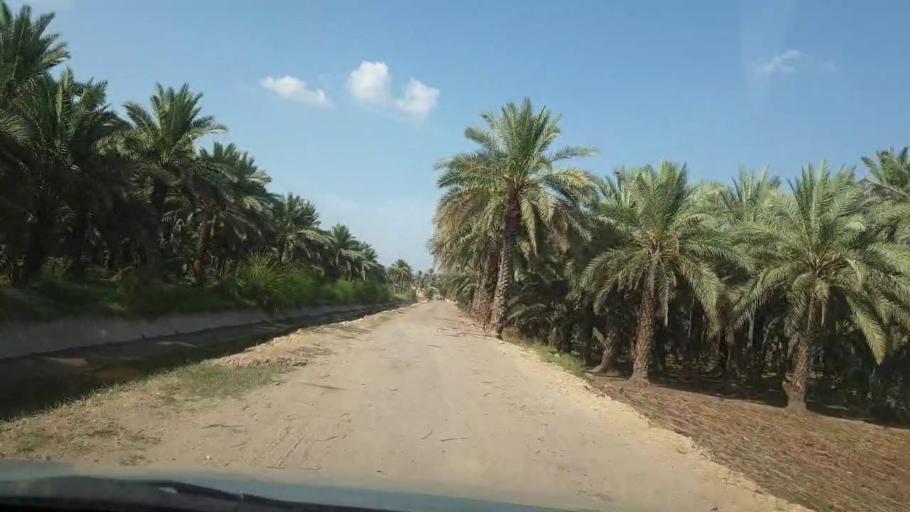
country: PK
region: Sindh
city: Sukkur
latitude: 27.6517
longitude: 68.8283
